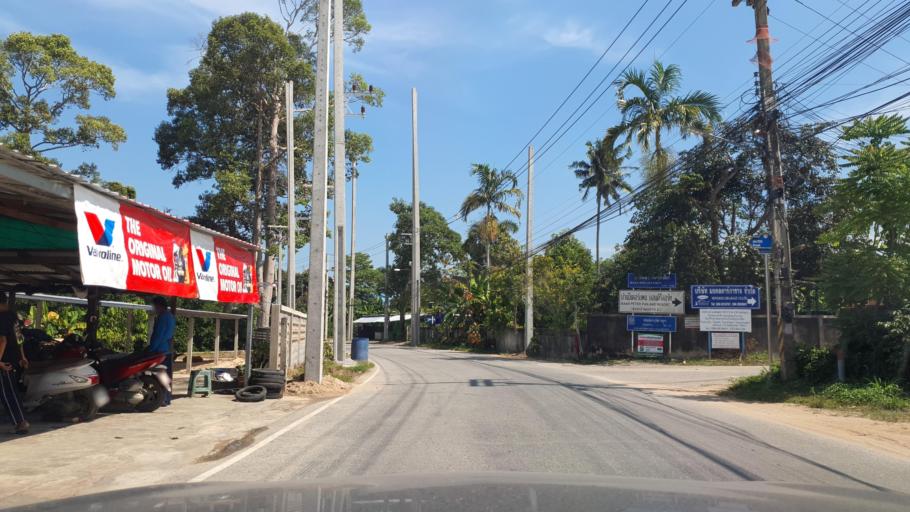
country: TH
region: Chon Buri
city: Bang Lamung
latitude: 12.9814
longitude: 100.9637
